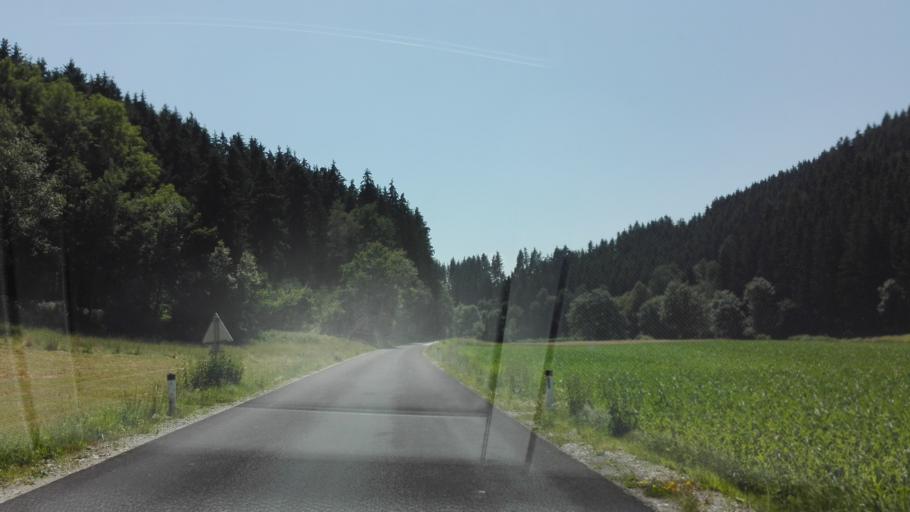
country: AT
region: Upper Austria
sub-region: Politischer Bezirk Grieskirchen
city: Bad Schallerbach
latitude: 48.3566
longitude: 13.8893
